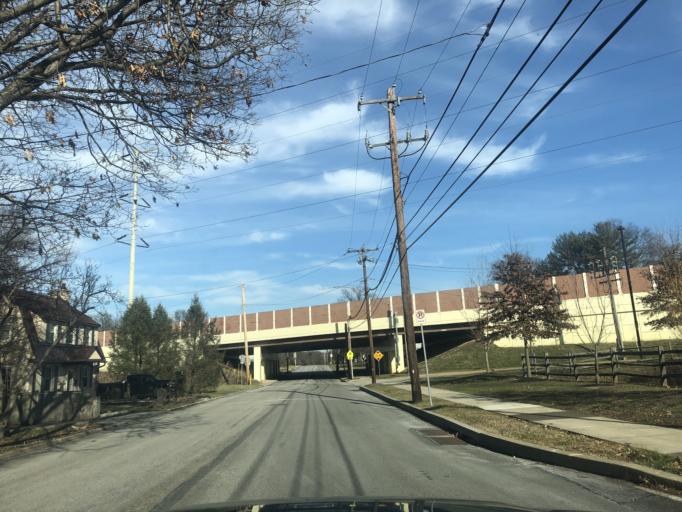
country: US
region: Pennsylvania
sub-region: Montgomery County
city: Flourtown
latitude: 40.1057
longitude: -75.1985
